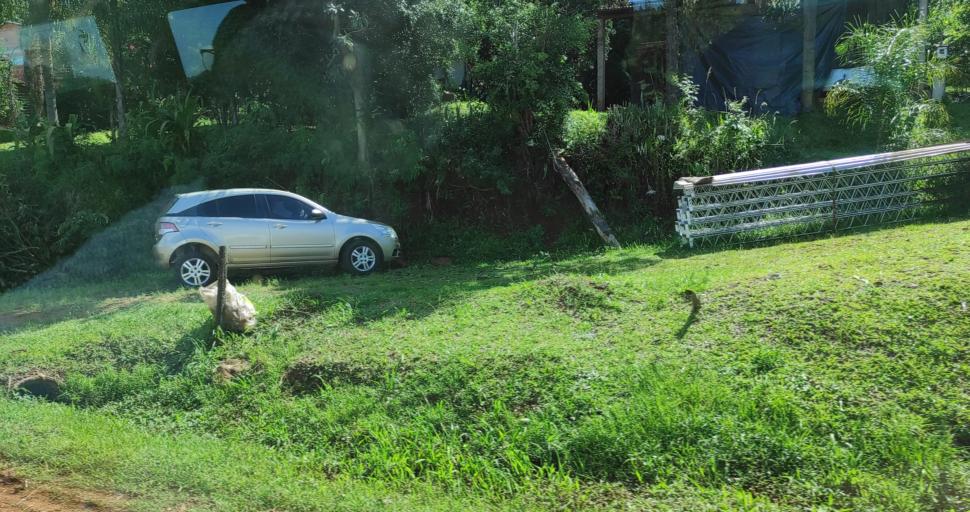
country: AR
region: Misiones
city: El Soberbio
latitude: -27.2895
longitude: -54.1986
